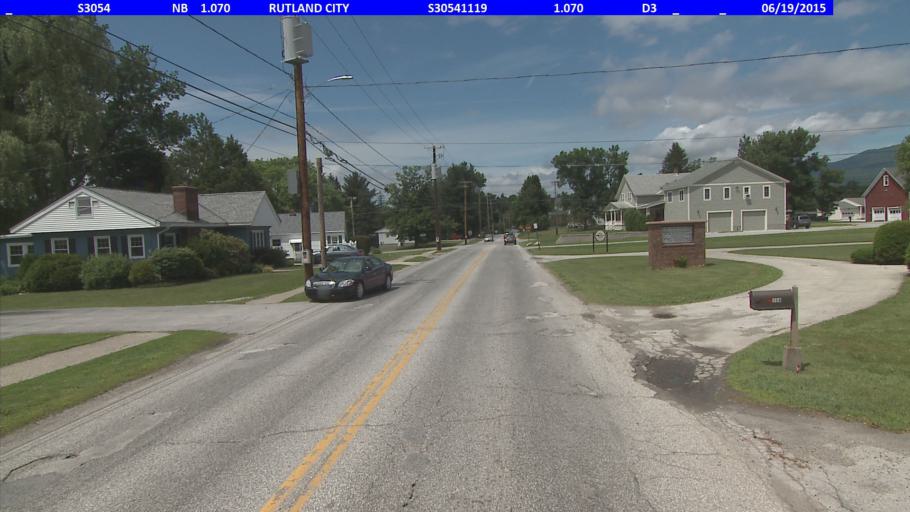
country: US
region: Vermont
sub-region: Rutland County
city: Rutland
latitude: 43.6067
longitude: -72.9562
